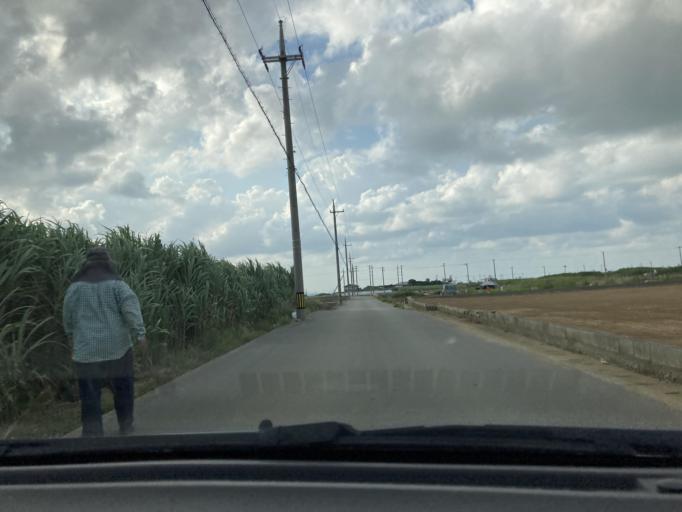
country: JP
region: Okinawa
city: Itoman
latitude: 26.0832
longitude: 127.6677
